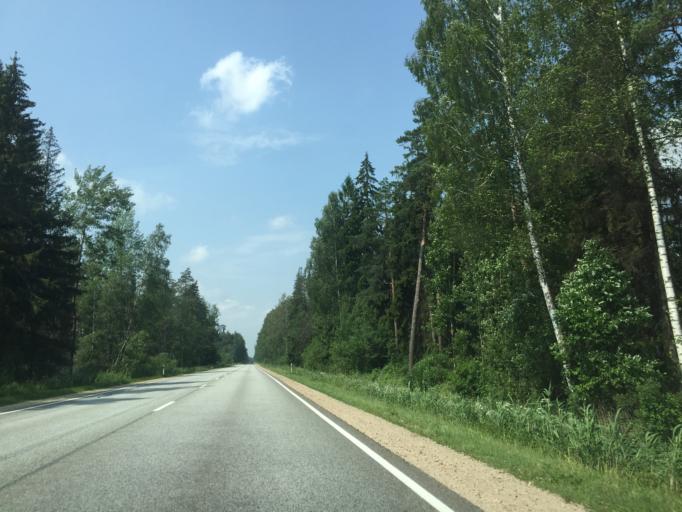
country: LV
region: Kekava
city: Balozi
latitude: 56.8150
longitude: 24.1366
